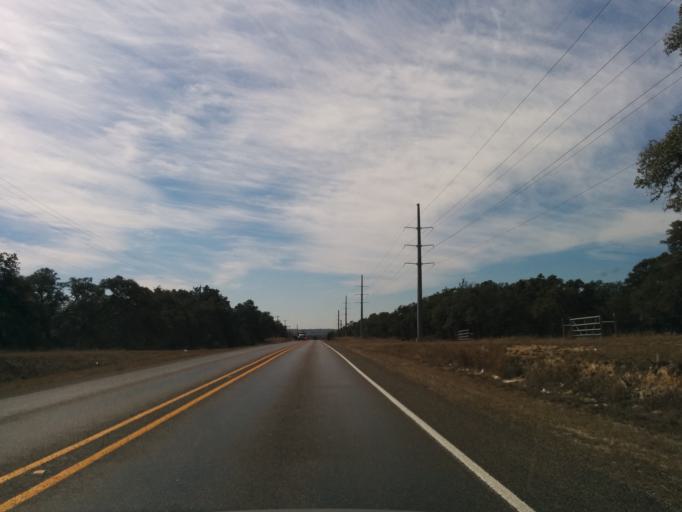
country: US
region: Texas
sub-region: Bexar County
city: Fair Oaks Ranch
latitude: 29.7661
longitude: -98.6082
